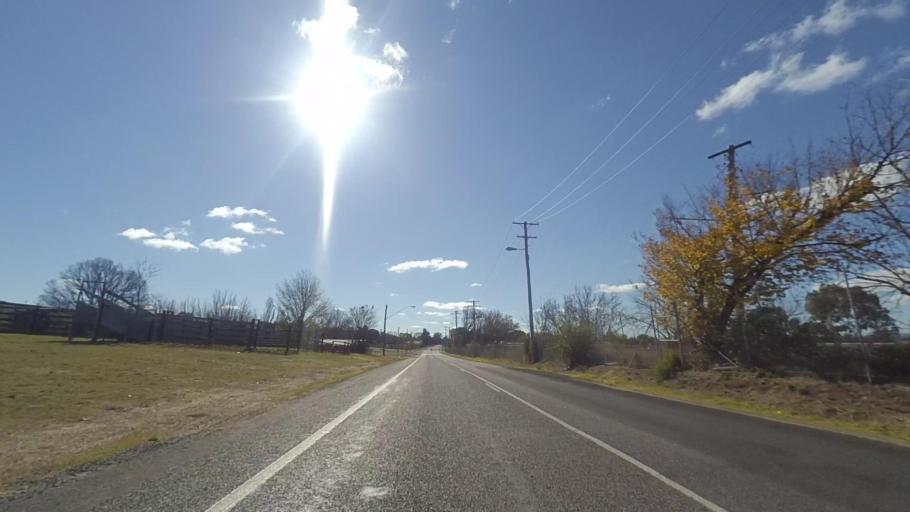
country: AU
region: New South Wales
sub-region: Bathurst Regional
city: Bathurst
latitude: -33.4423
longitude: 149.5787
